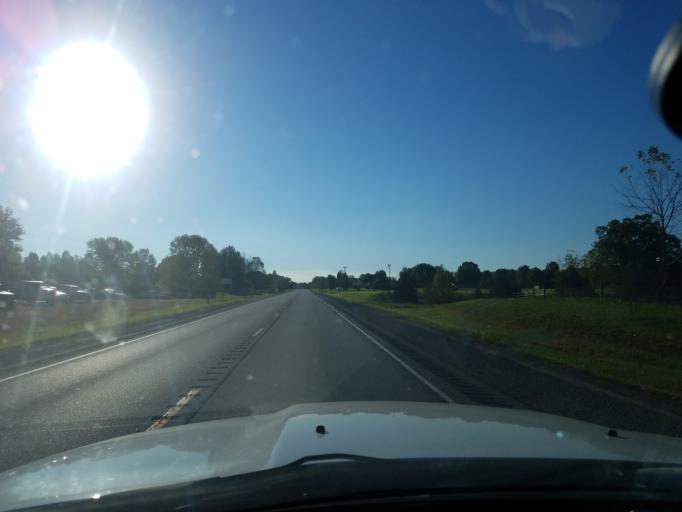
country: US
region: Kentucky
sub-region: Nelson County
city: Bardstown
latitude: 37.8859
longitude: -85.5487
